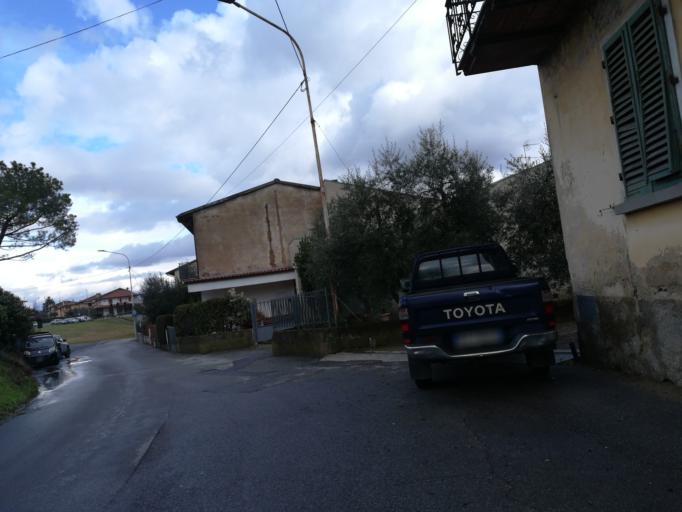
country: IT
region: Tuscany
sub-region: Provincia di Prato
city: Poggio A Caiano
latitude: 43.8084
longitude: 11.0521
